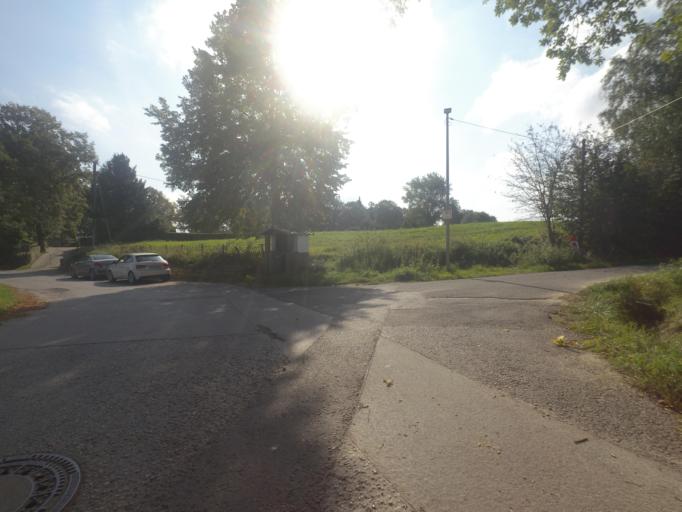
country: DE
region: North Rhine-Westphalia
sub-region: Regierungsbezirk Arnsberg
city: Frondenberg
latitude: 51.4571
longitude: 7.7282
